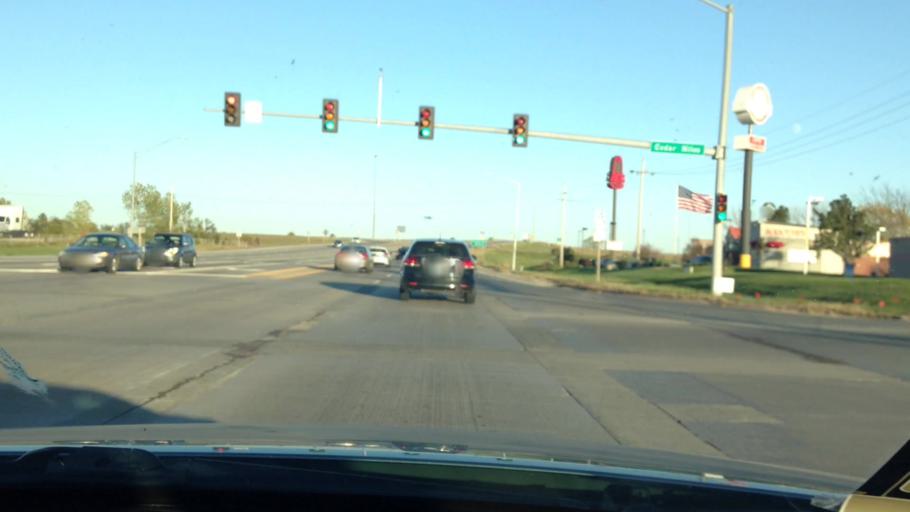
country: US
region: Kansas
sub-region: Johnson County
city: Gardner
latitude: 38.8118
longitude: -94.8906
